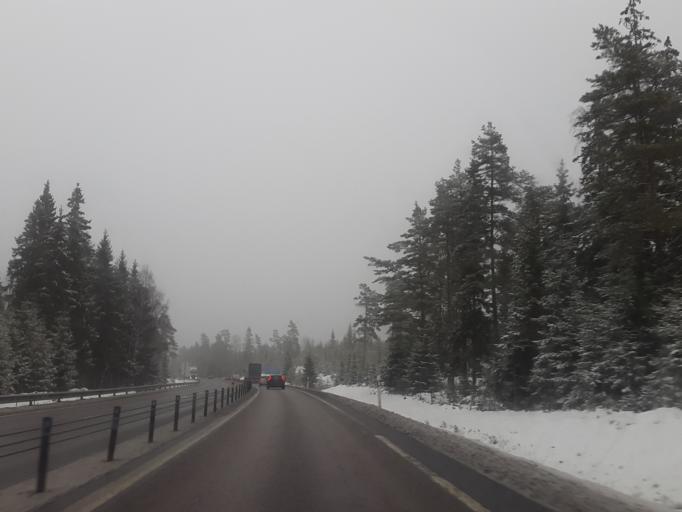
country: SE
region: Joenkoeping
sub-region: Jonkopings Kommun
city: Taberg
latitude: 57.7521
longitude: 13.9820
